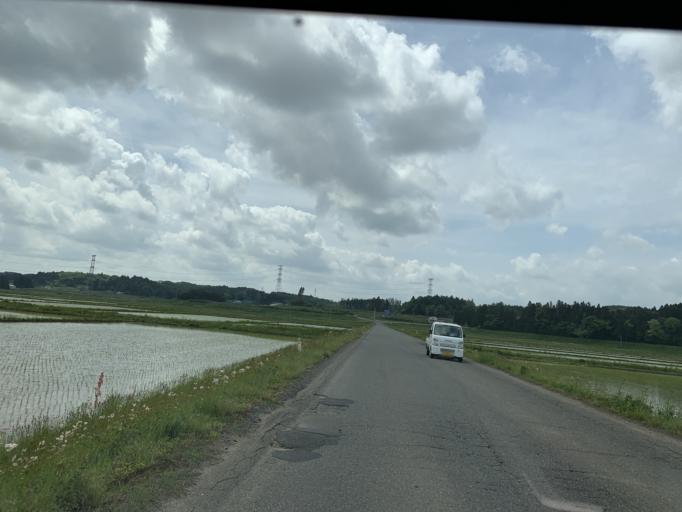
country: JP
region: Iwate
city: Ichinoseki
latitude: 38.8211
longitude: 141.0202
